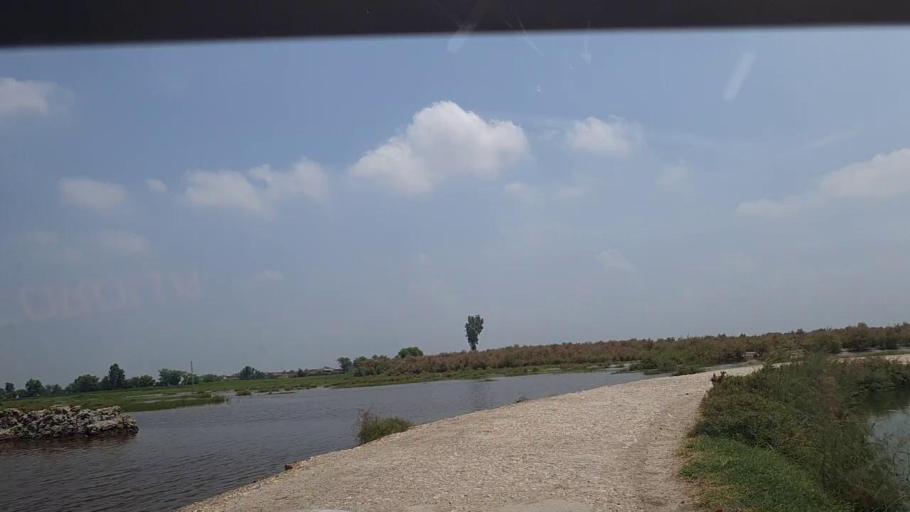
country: PK
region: Sindh
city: Khanpur
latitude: 27.8959
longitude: 69.3968
